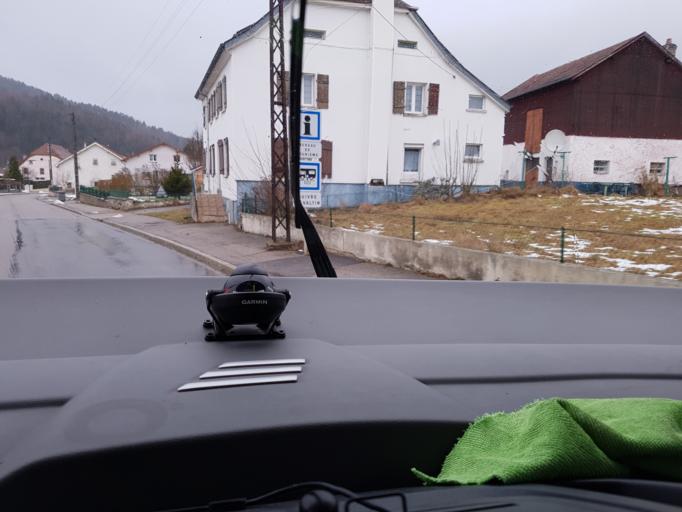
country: FR
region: Lorraine
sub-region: Departement des Vosges
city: Plainfaing
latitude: 48.1707
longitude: 7.0196
